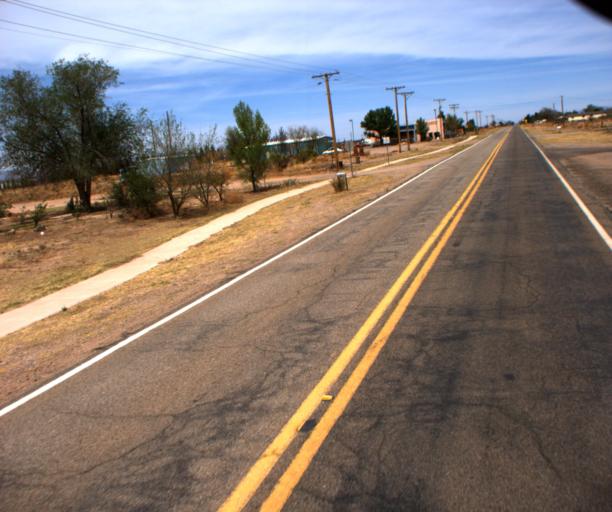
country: US
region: Arizona
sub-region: Cochise County
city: Bisbee
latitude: 31.6954
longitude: -109.6872
